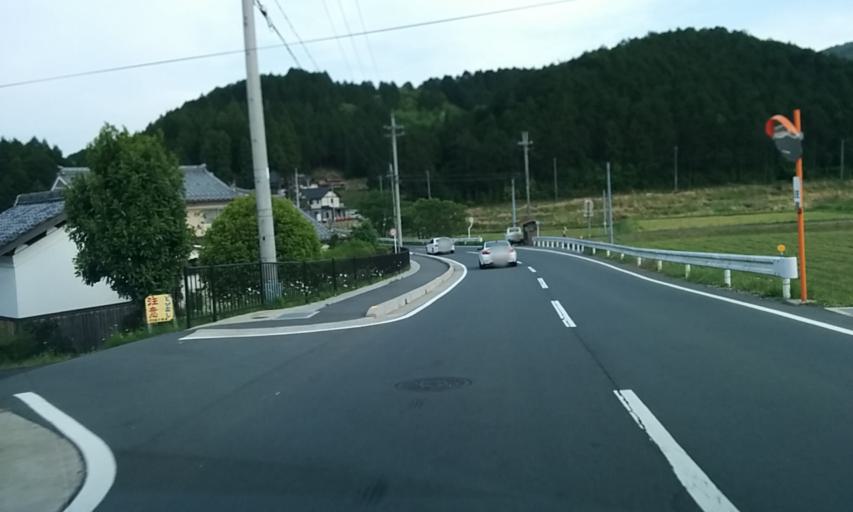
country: JP
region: Kyoto
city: Ayabe
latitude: 35.1681
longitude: 135.3870
